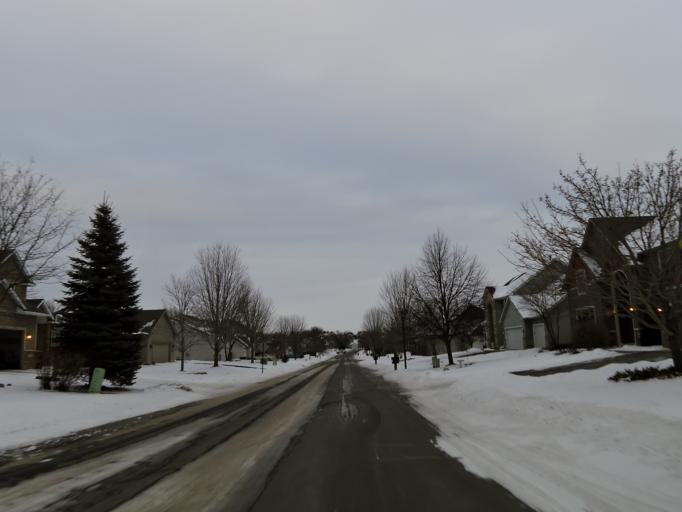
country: US
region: Minnesota
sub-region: Washington County
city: Woodbury
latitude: 44.9121
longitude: -92.8932
